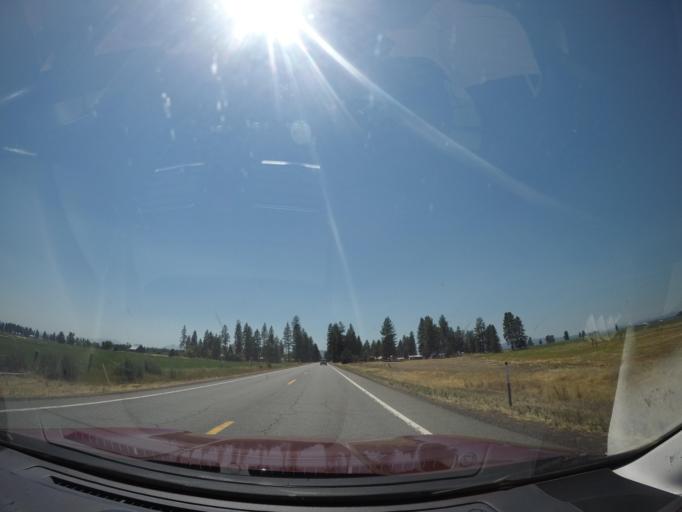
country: US
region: California
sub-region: Shasta County
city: Burney
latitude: 41.0691
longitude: -121.3435
